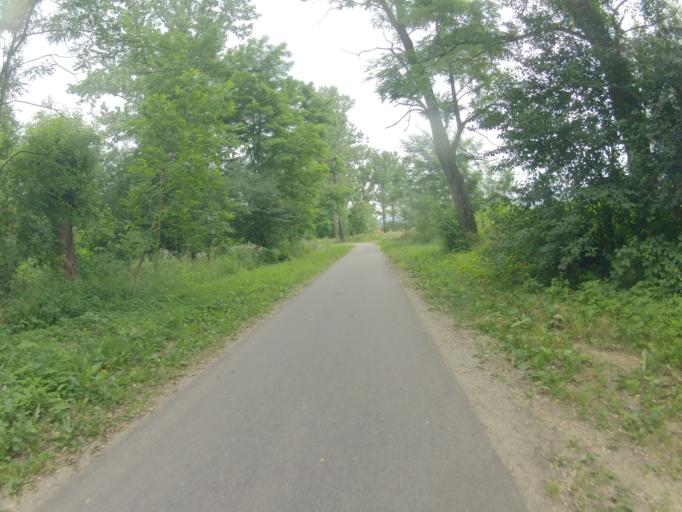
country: PL
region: Lesser Poland Voivodeship
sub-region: Powiat nowosadecki
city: Stary Sacz
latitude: 49.5376
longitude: 20.6582
